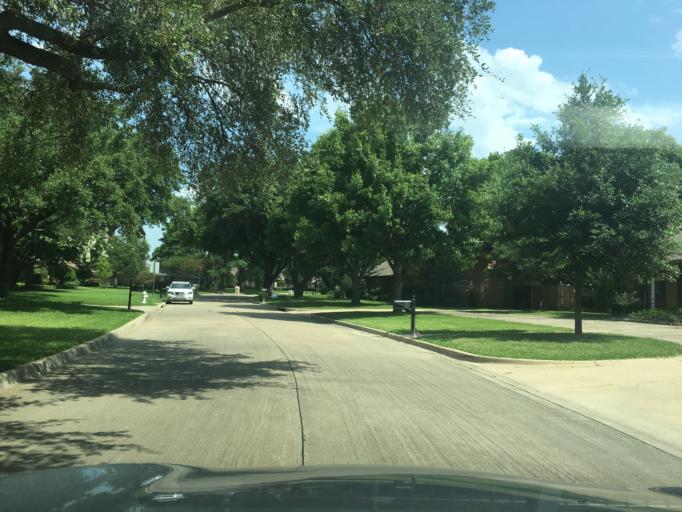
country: US
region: Texas
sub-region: Dallas County
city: Farmers Branch
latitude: 32.9319
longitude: -96.8565
